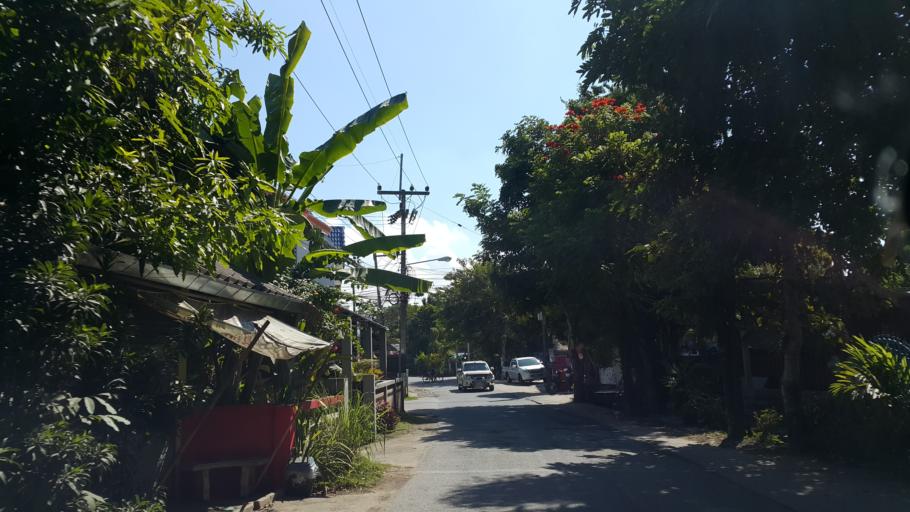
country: TH
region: Chiang Mai
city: San Sai
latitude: 18.8365
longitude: 99.0180
